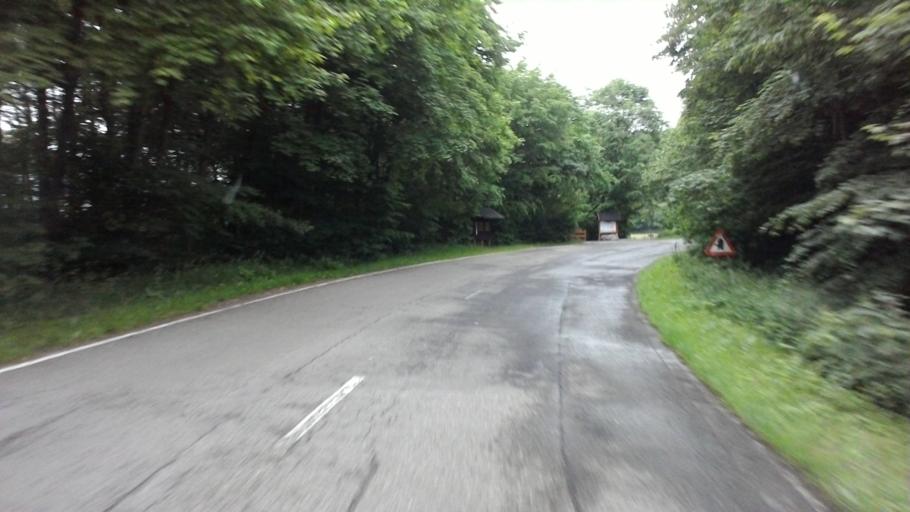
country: BE
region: Wallonia
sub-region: Province de Liege
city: Eupen
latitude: 50.6221
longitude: 6.0701
